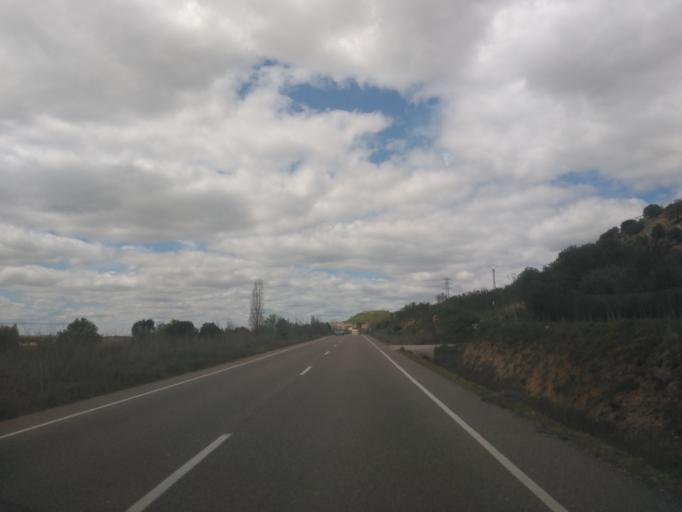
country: ES
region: Castille and Leon
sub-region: Provincia de Salamanca
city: Almenara de Tormes
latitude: 41.0600
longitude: -5.8103
